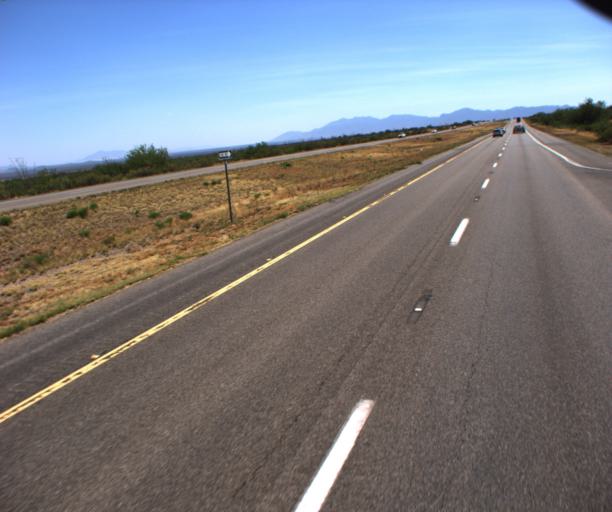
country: US
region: Arizona
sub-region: Cochise County
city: Whetstone
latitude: 31.8330
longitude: -110.3443
